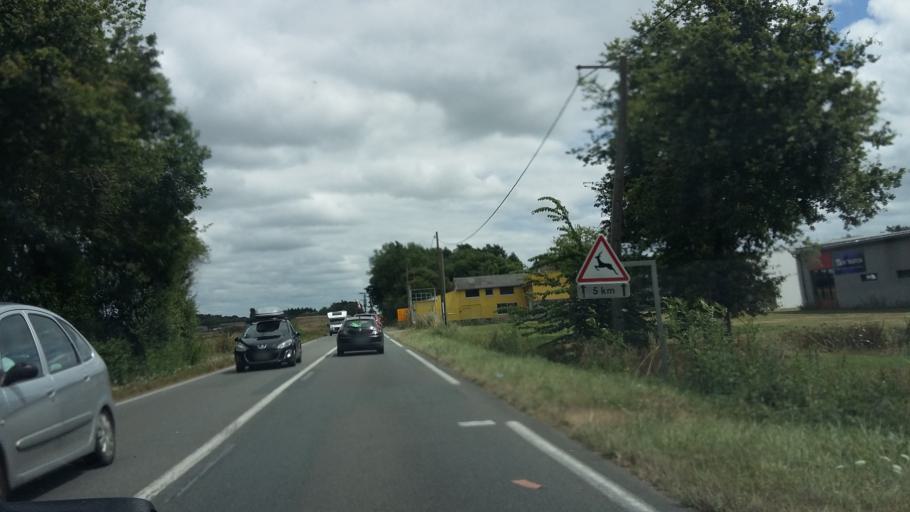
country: FR
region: Pays de la Loire
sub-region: Departement de la Vendee
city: Challans
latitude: 46.8367
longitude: -1.8403
